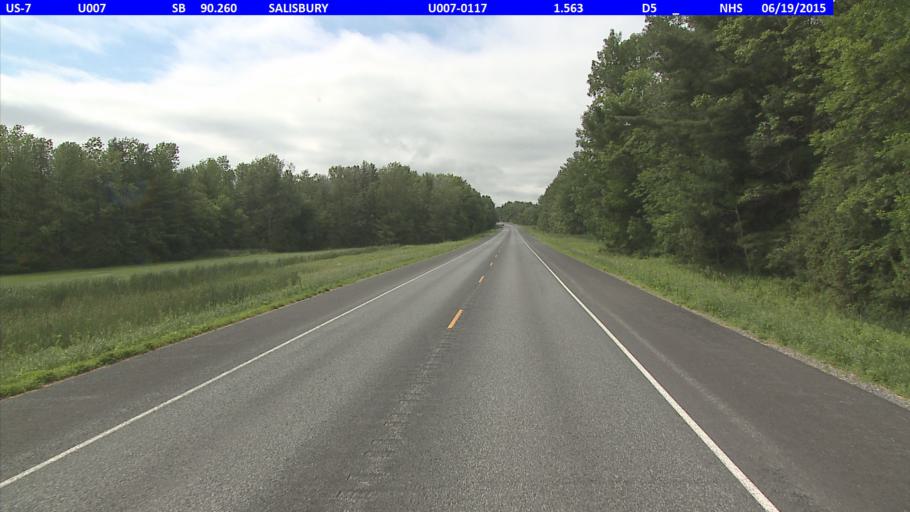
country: US
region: Vermont
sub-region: Addison County
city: Middlebury (village)
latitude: 43.9155
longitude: -73.1116
